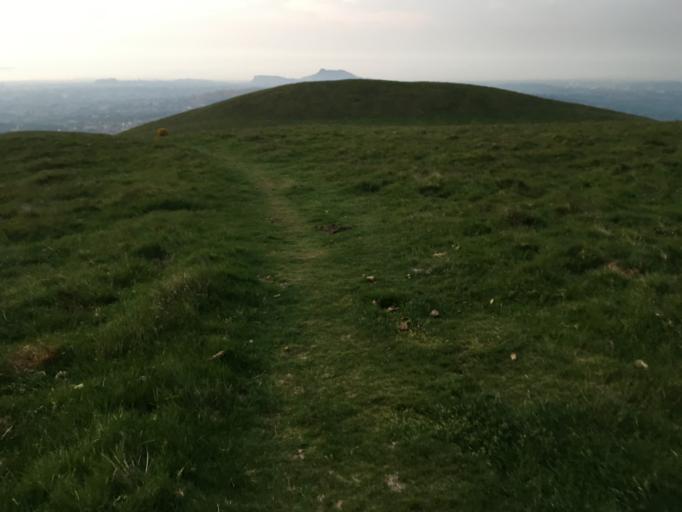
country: GB
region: Scotland
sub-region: Edinburgh
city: Colinton
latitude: 55.8870
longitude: -3.2258
